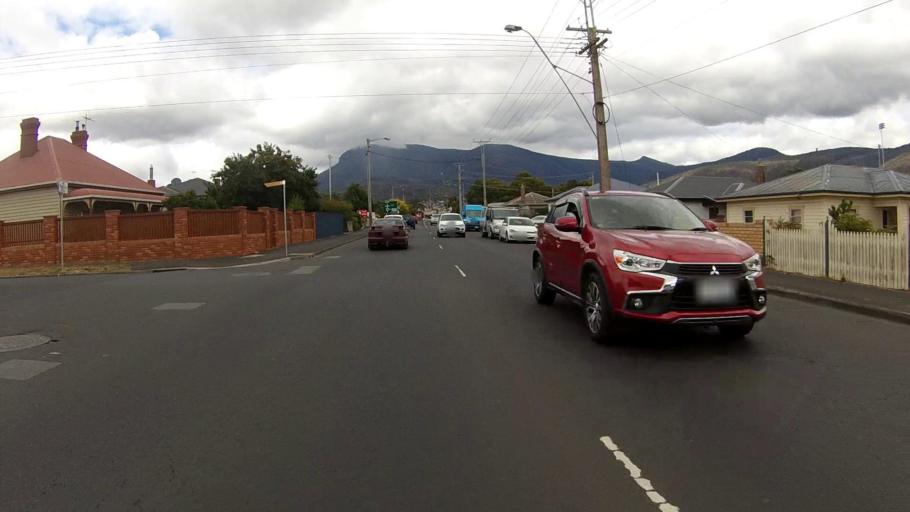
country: AU
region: Tasmania
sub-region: Glenorchy
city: Glenorchy
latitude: -42.8314
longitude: 147.2811
